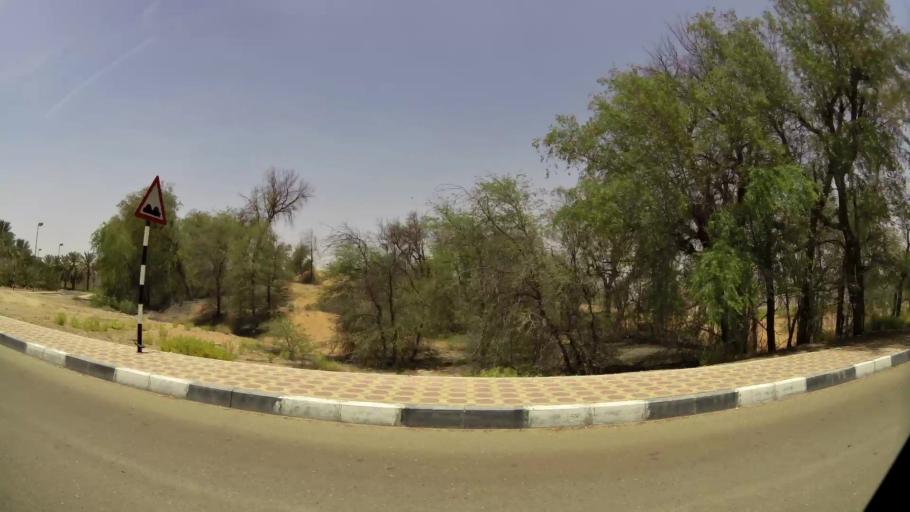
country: OM
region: Al Buraimi
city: Al Buraymi
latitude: 24.2746
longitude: 55.7283
